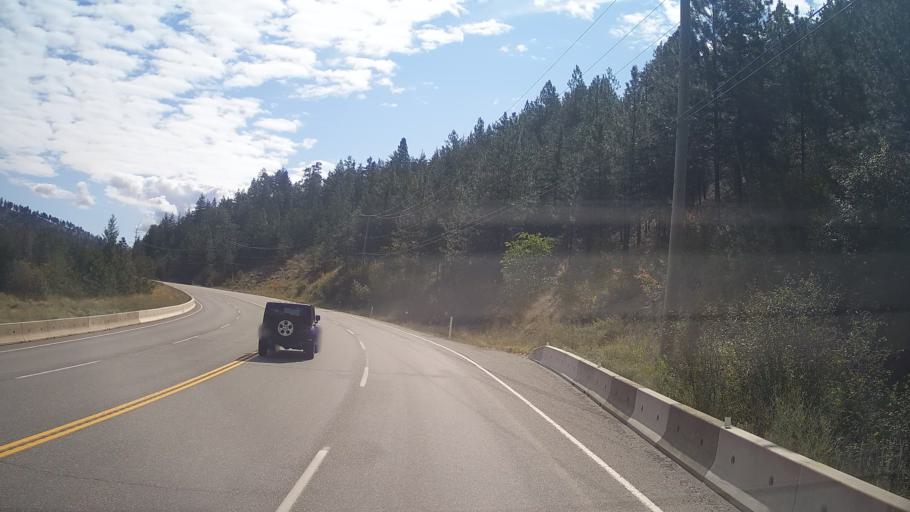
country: CA
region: British Columbia
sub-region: Thompson-Nicola Regional District
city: Ashcroft
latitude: 50.2542
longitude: -121.5175
